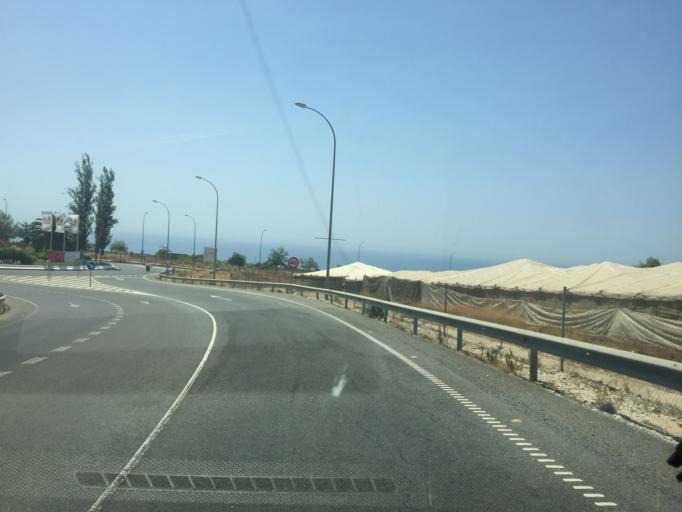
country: ES
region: Andalusia
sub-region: Provincia de Malaga
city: Nerja
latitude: 36.7568
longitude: -3.8526
